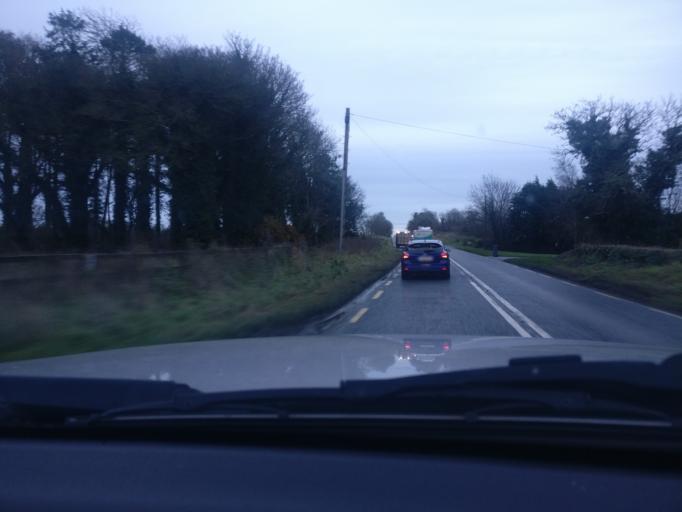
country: IE
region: Leinster
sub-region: An Mhi
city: Kells
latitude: 53.7111
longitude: -6.8137
